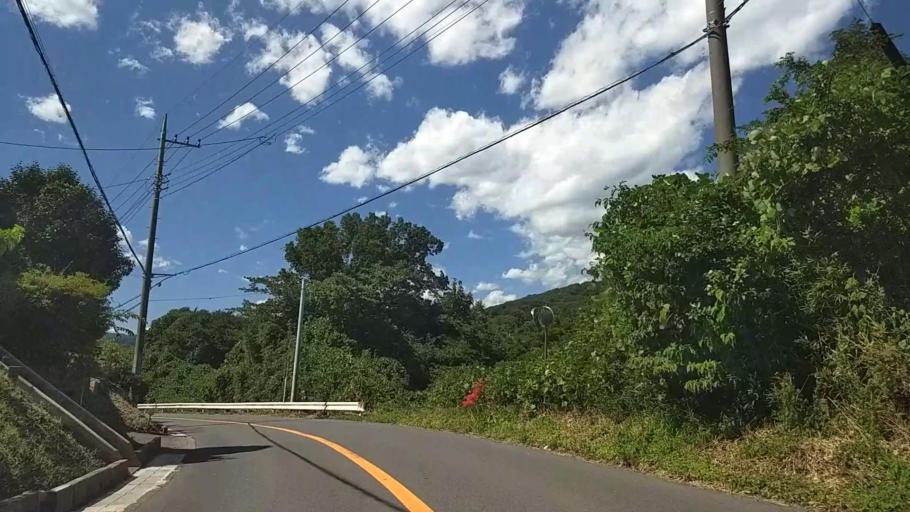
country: JP
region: Kanagawa
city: Zama
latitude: 35.5339
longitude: 139.3196
